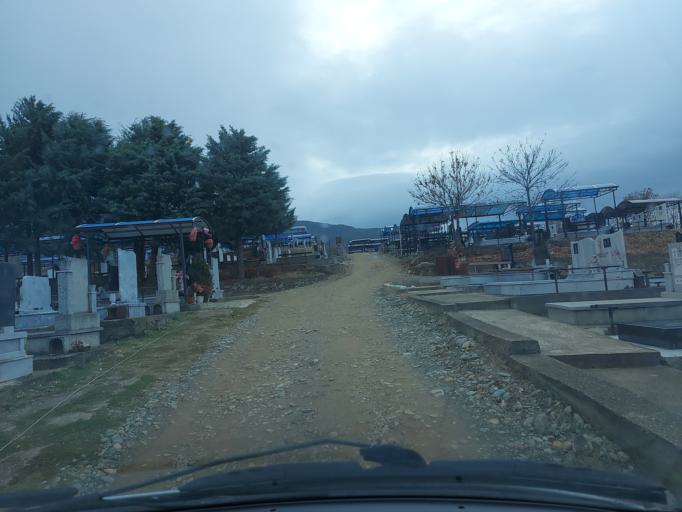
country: MK
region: Kriva Palanka
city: Kriva Palanka
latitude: 42.1875
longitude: 22.2945
